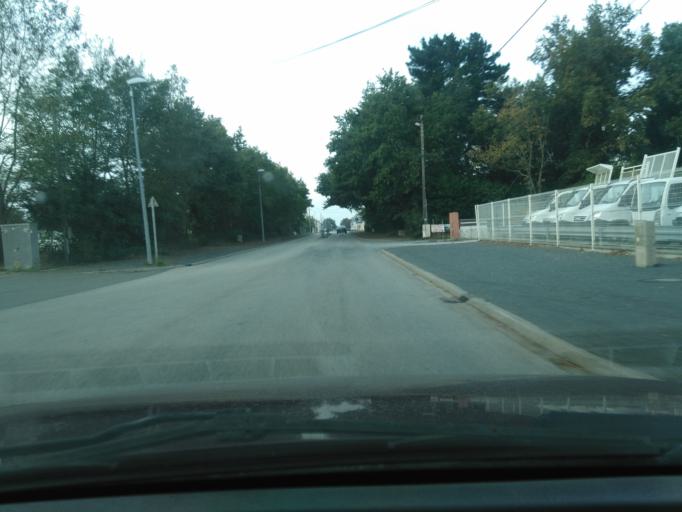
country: FR
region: Pays de la Loire
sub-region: Departement de la Vendee
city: Mouilleron-le-Captif
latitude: 46.7294
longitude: -1.4299
